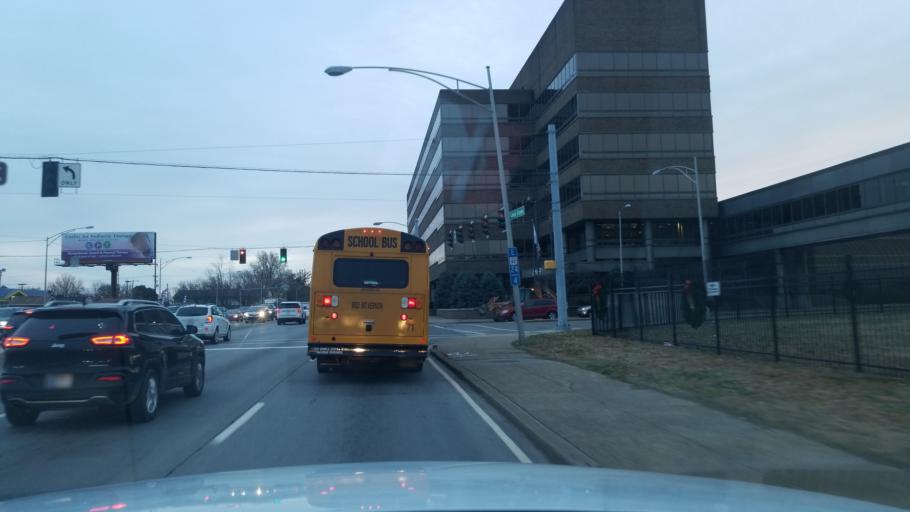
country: US
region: Indiana
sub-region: Vanderburgh County
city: Evansville
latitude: 37.9778
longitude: -87.6011
